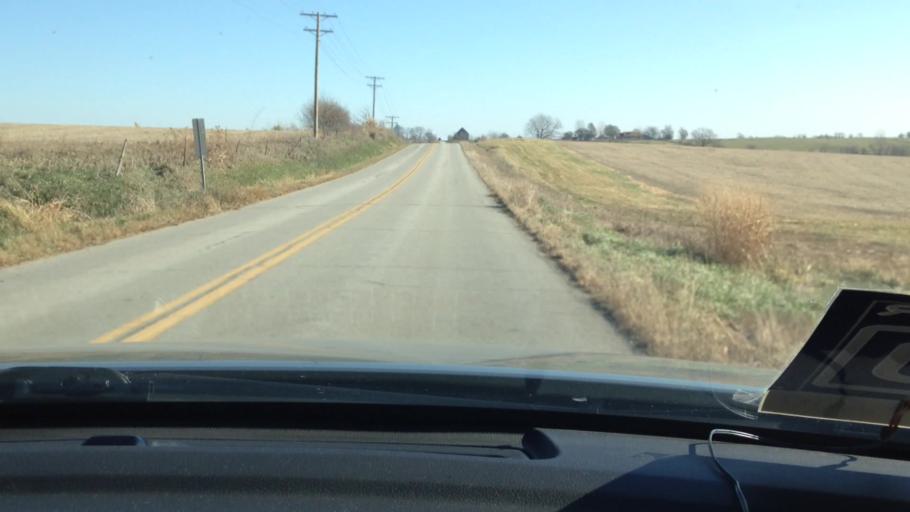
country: US
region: Missouri
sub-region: Platte County
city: Weston
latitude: 39.4832
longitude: -94.8901
